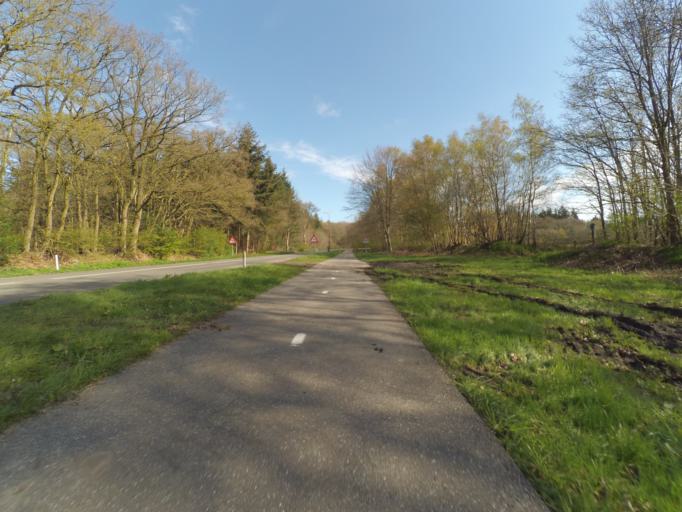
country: NL
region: Gelderland
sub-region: Gemeente Apeldoorn
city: Uddel
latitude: 52.3012
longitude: 5.7853
